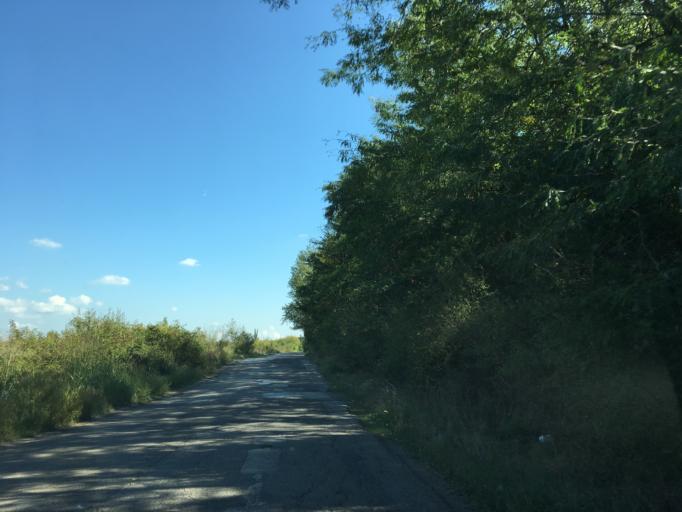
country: RO
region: Dolj
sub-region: Comuna Desa
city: Desa
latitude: 43.7643
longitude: 23.0295
